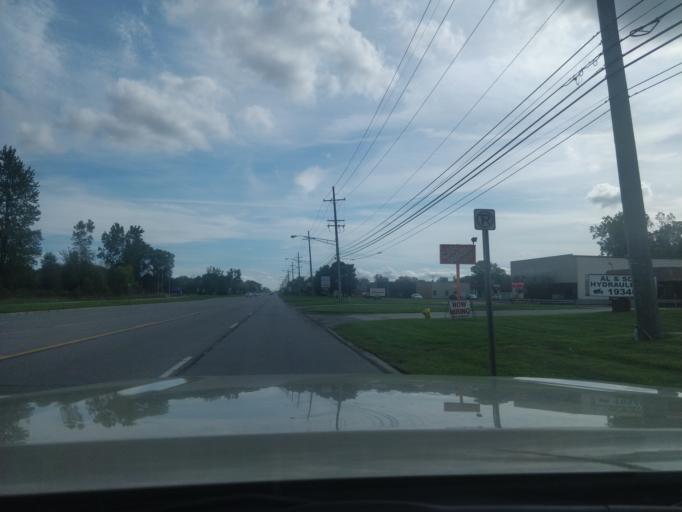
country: US
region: Michigan
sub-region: Wayne County
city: Woodhaven
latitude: 42.1643
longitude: -83.2270
